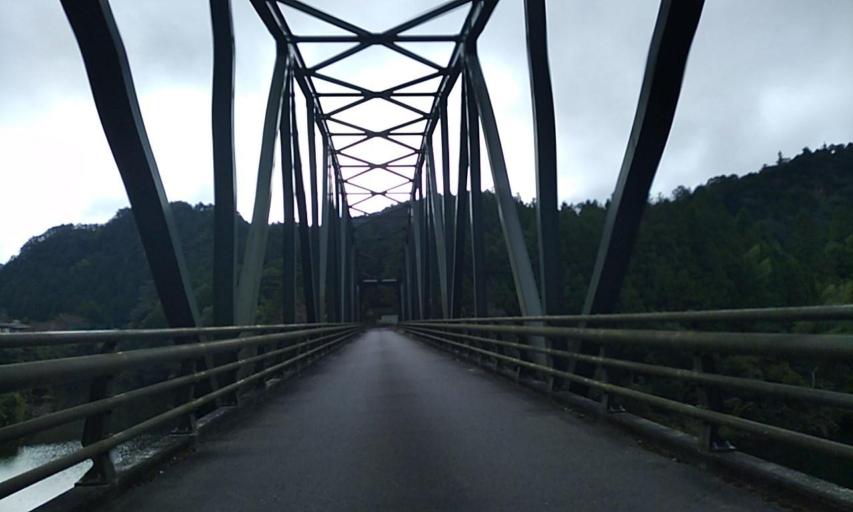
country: JP
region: Wakayama
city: Shingu
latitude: 33.9339
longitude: 135.9711
